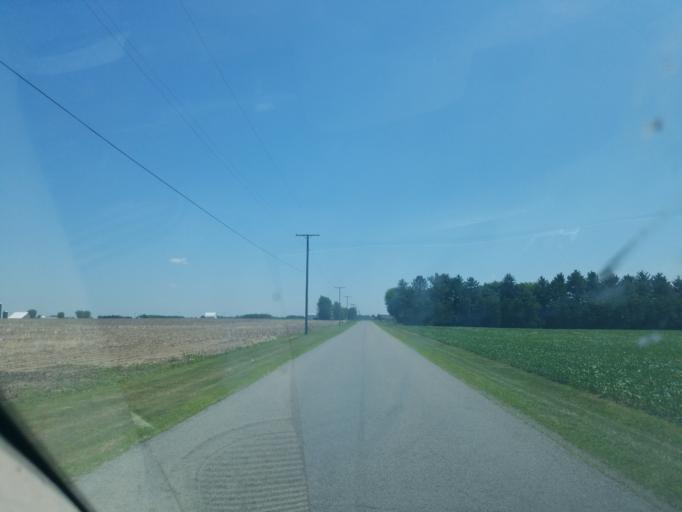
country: US
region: Ohio
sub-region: Allen County
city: Spencerville
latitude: 40.7575
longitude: -84.3683
